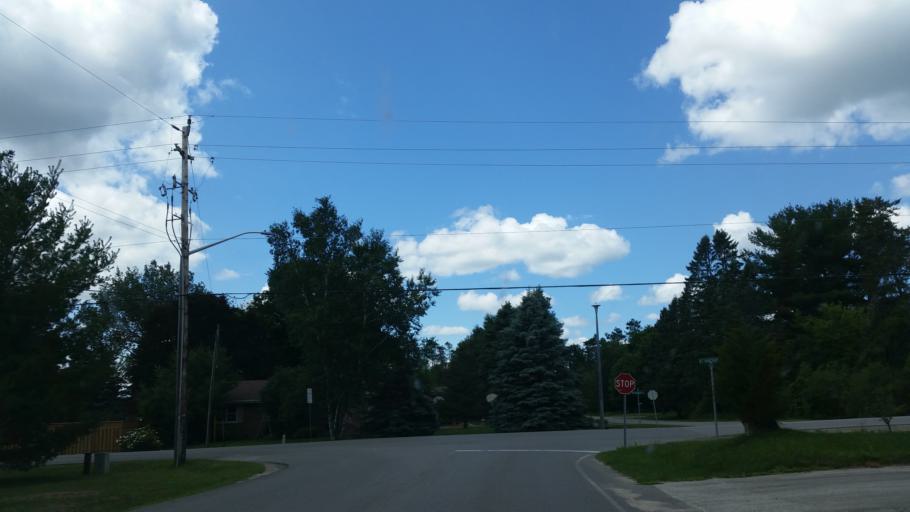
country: CA
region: Ontario
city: Barrie
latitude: 44.4454
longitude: -79.7215
